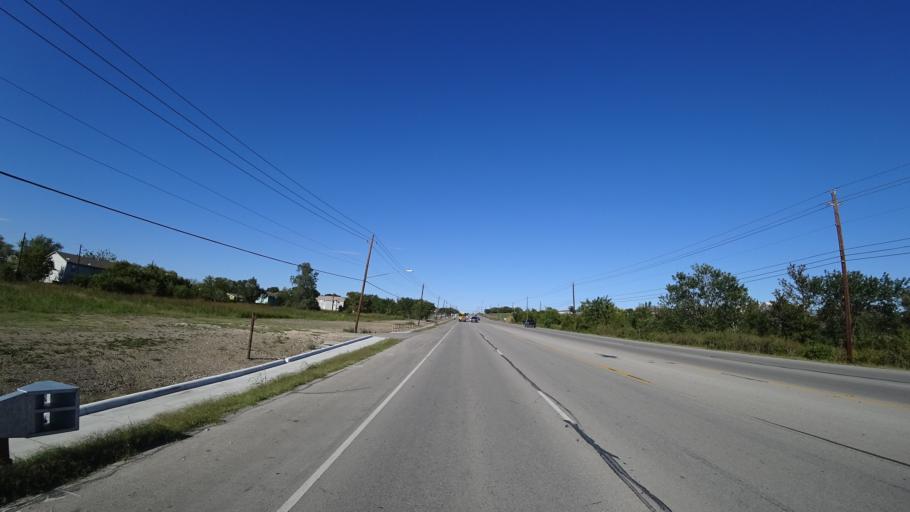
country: US
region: Texas
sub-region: Travis County
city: Hornsby Bend
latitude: 30.2926
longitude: -97.6271
